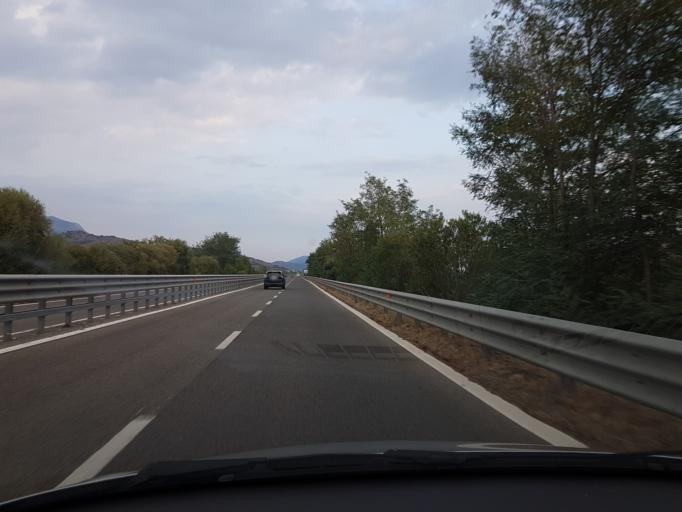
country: IT
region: Sardinia
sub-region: Provincia di Nuoro
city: Orune
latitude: 40.3854
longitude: 9.4458
